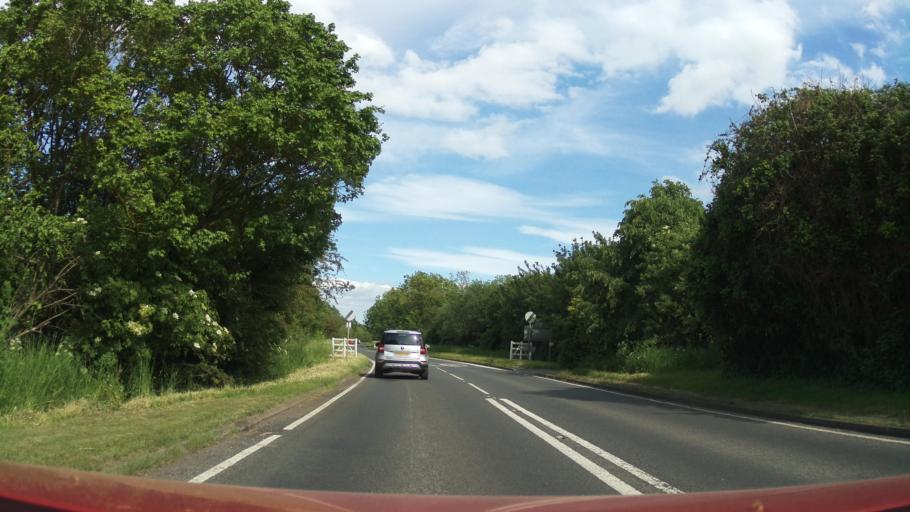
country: GB
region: England
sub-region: Worcestershire
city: Evesham
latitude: 52.0941
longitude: -1.9992
